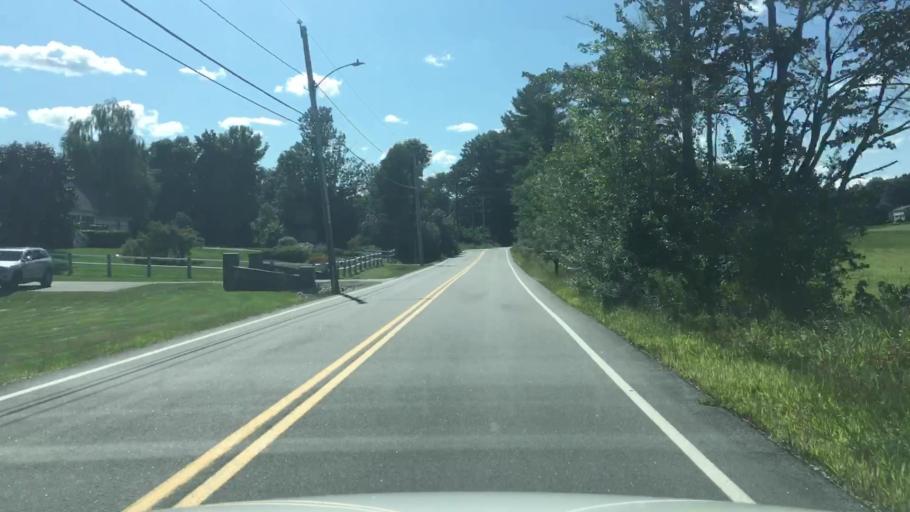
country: US
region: New Hampshire
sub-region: Strafford County
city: Dover
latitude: 43.1853
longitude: -70.8515
